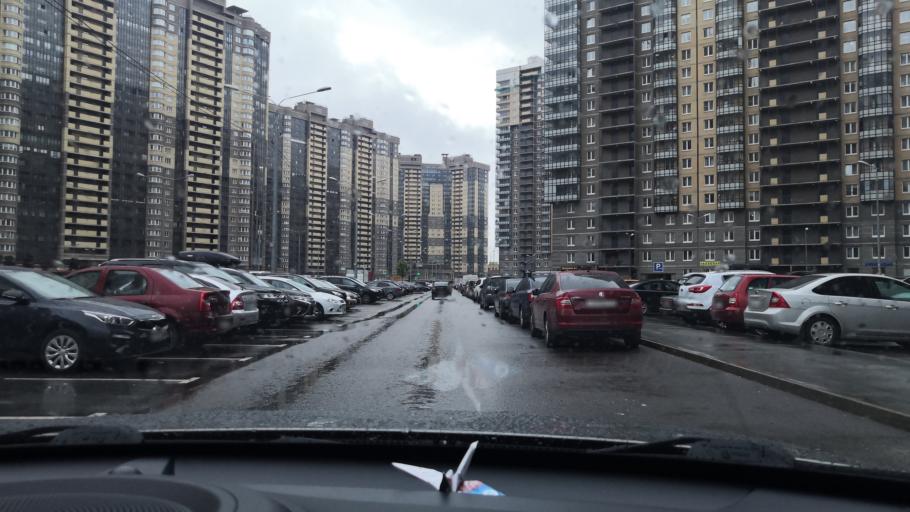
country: RU
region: Leningrad
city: Parnas
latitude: 60.0812
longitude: 30.3419
